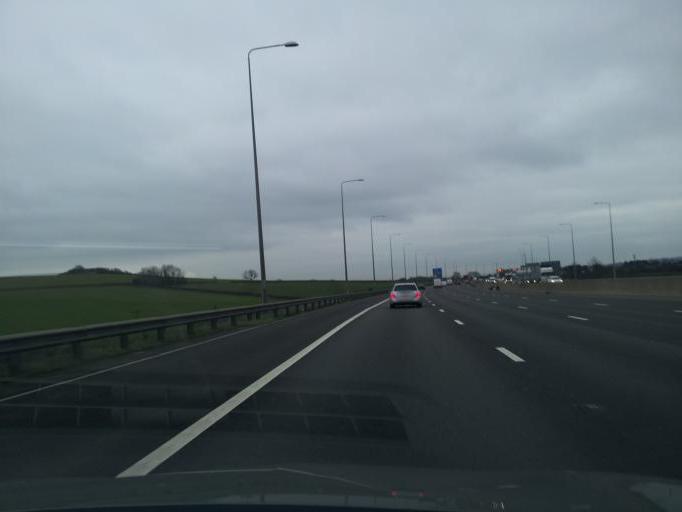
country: GB
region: England
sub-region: Nottinghamshire
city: Kimberley
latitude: 52.9722
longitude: -1.2539
